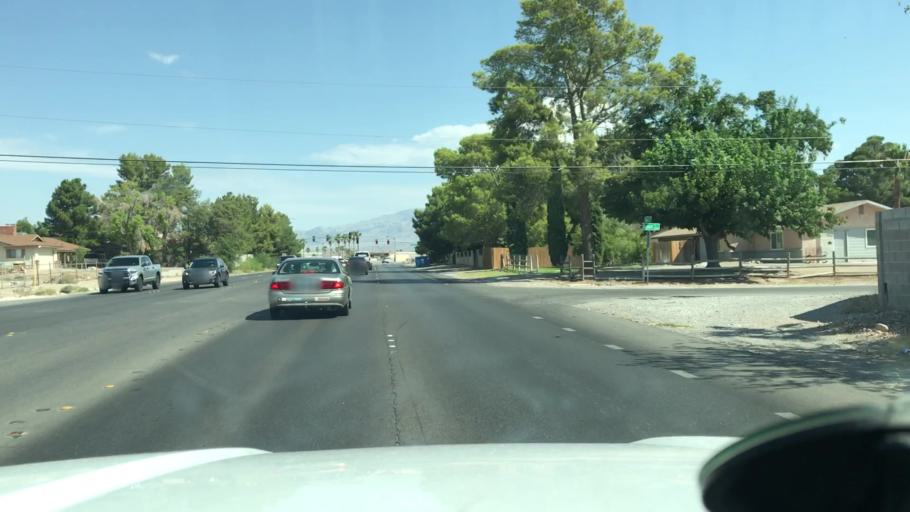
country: US
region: Nevada
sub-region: Clark County
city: Summerlin South
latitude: 36.2682
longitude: -115.2788
